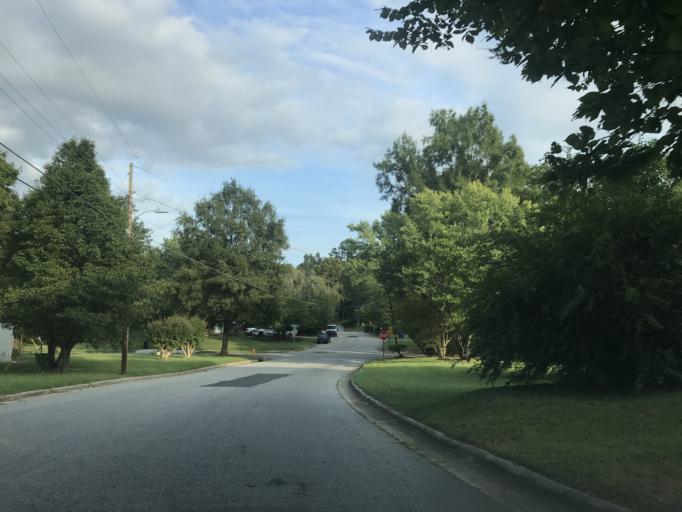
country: US
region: North Carolina
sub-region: Wake County
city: Raleigh
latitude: 35.7495
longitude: -78.6236
